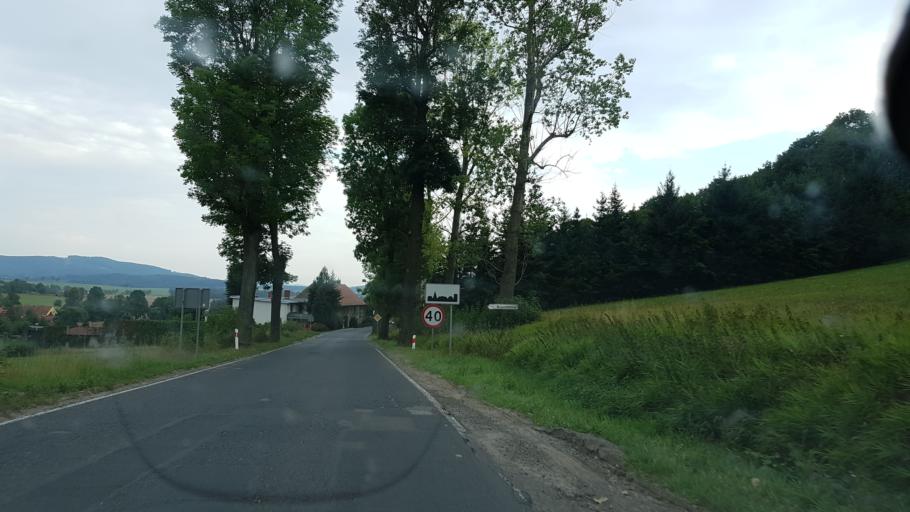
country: PL
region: Lower Silesian Voivodeship
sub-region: Powiat kamiennogorski
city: Marciszow
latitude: 50.8875
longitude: 15.9952
